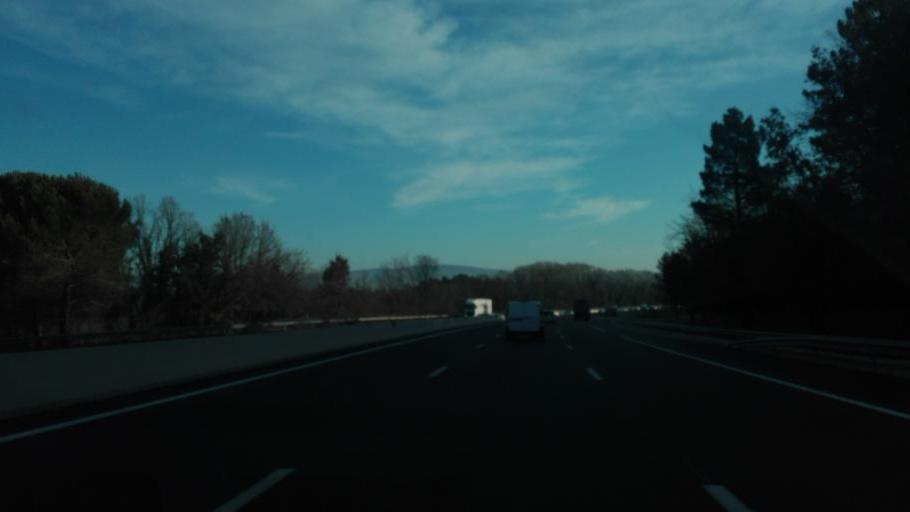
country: FR
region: Provence-Alpes-Cote d'Azur
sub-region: Departement du Var
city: La Motte
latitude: 43.4546
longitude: 6.5261
